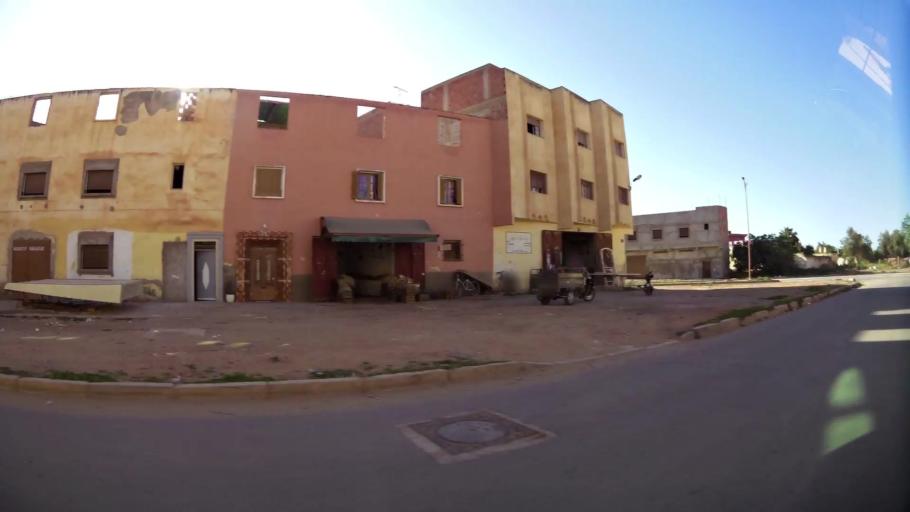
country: MA
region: Oriental
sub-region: Berkane-Taourirt
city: Berkane
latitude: 34.9336
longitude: -2.3423
